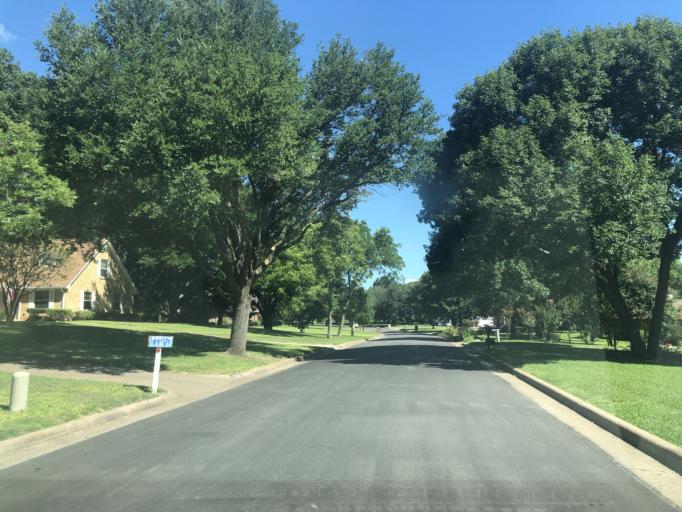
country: US
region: Texas
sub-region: Dallas County
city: Duncanville
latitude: 32.6369
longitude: -96.9377
